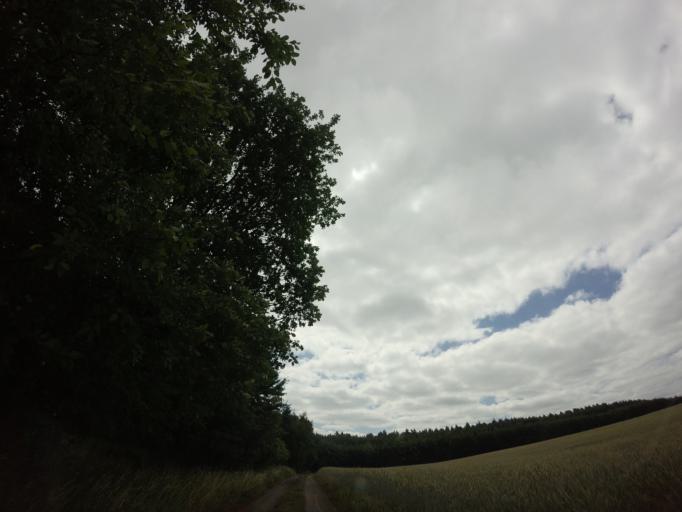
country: PL
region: West Pomeranian Voivodeship
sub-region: Powiat choszczenski
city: Krzecin
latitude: 53.0228
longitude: 15.5421
